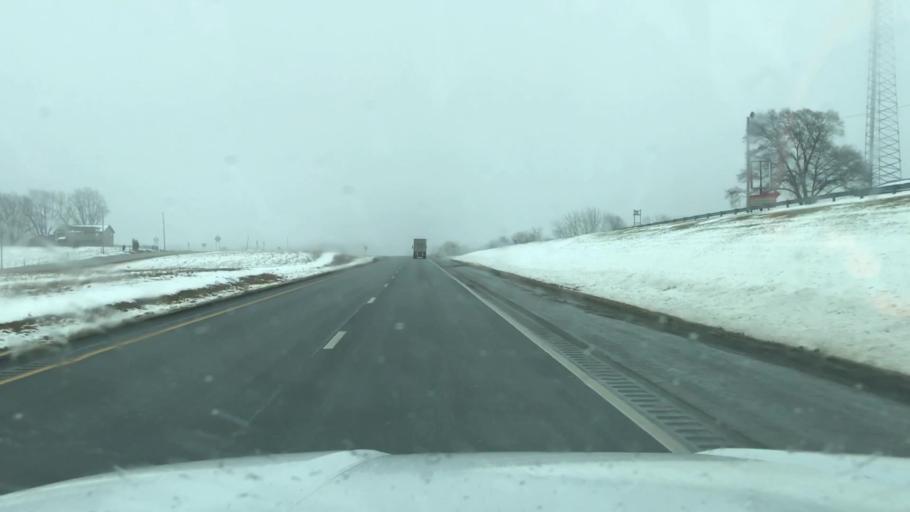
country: US
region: Missouri
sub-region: Clinton County
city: Gower
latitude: 39.7620
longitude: -94.4968
